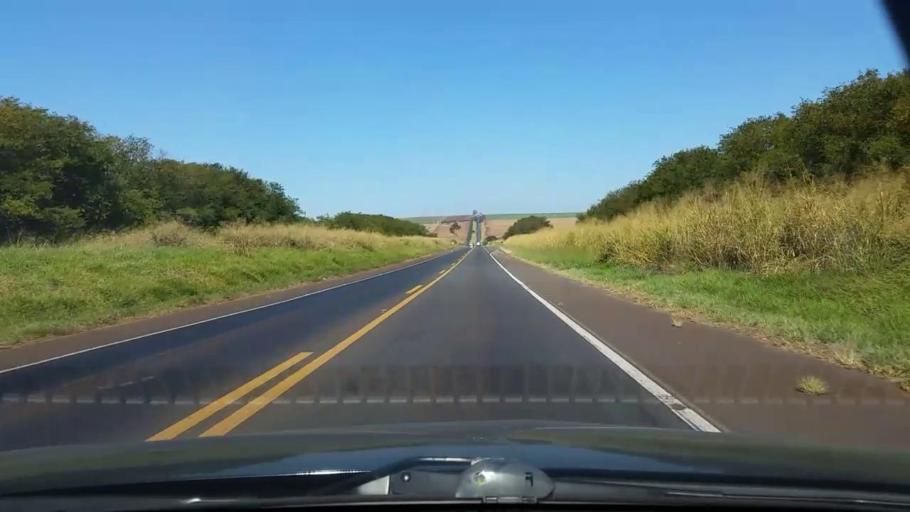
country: BR
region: Sao Paulo
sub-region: Jau
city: Jau
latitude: -22.3660
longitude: -48.5711
